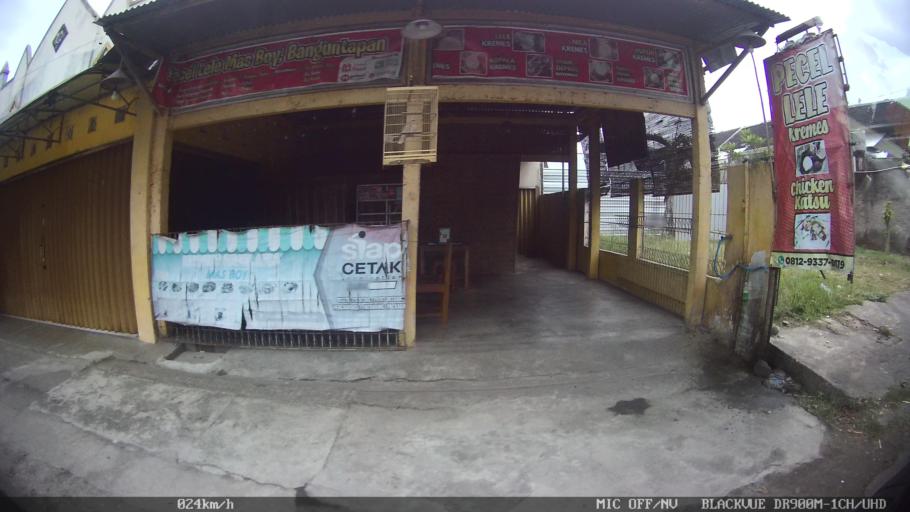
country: ID
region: Daerah Istimewa Yogyakarta
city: Depok
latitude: -7.8155
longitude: 110.4168
